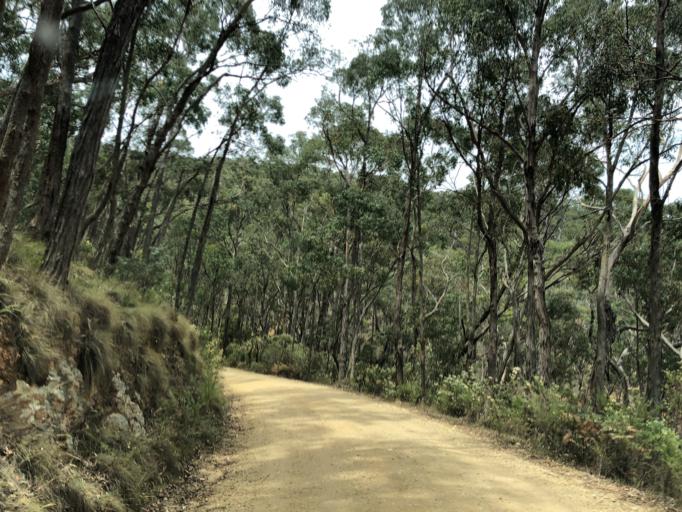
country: AU
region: Victoria
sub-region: Moorabool
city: Bacchus Marsh
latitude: -37.4928
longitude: 144.3657
